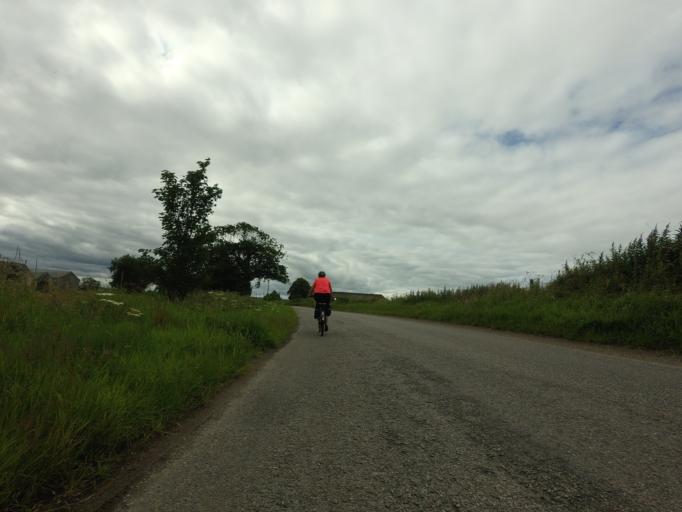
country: GB
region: Scotland
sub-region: Moray
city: Forres
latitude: 57.6225
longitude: -3.6130
